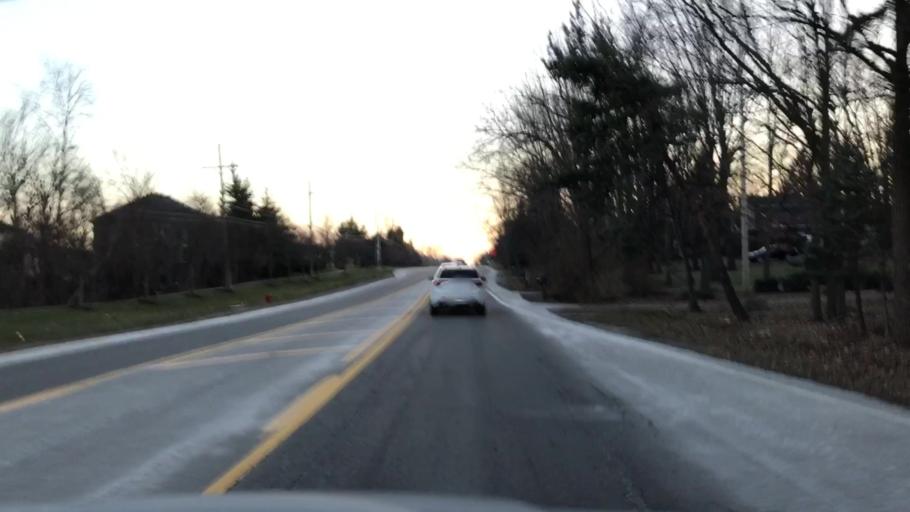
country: US
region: Michigan
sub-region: Wayne County
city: Northville
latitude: 42.4566
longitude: -83.5138
